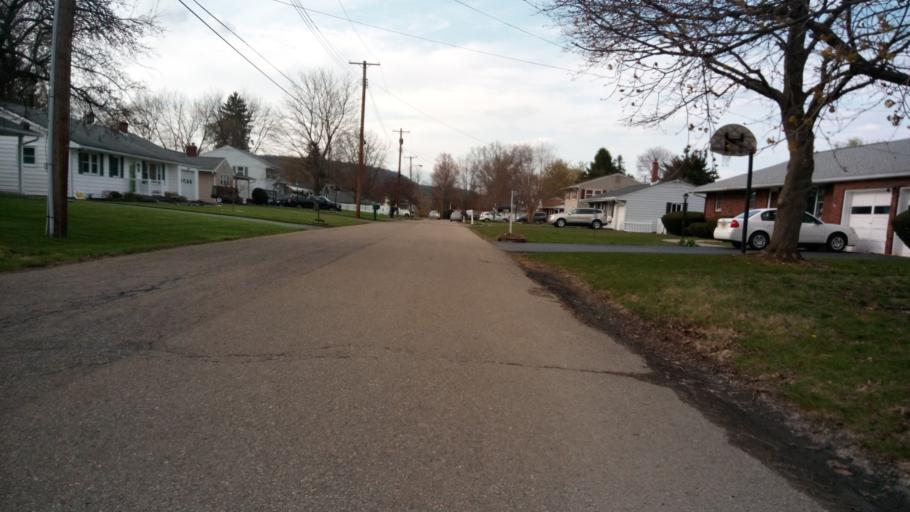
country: US
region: New York
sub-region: Chemung County
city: Southport
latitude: 42.0733
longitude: -76.8232
